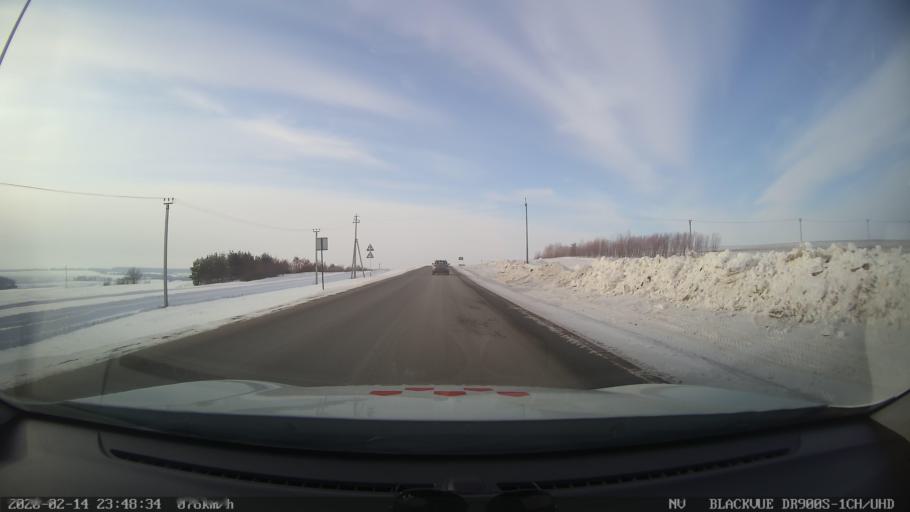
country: RU
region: Tatarstan
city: Kuybyshevskiy Zaton
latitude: 55.2485
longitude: 49.2005
